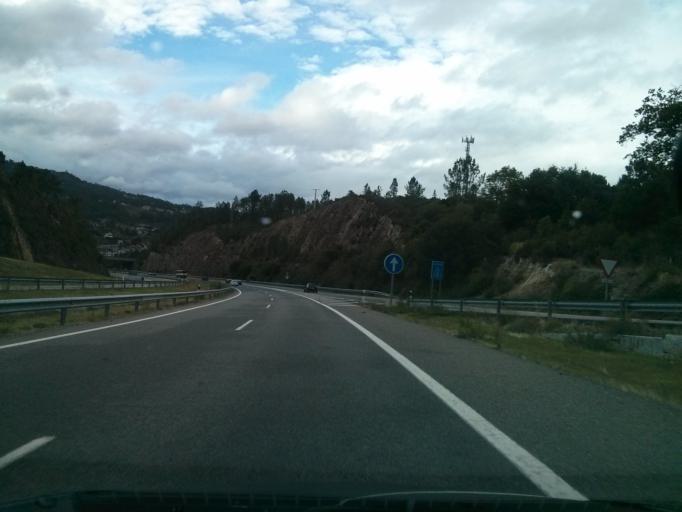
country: ES
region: Galicia
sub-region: Provincia de Ourense
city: Ourense
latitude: 42.3079
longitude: -7.8757
